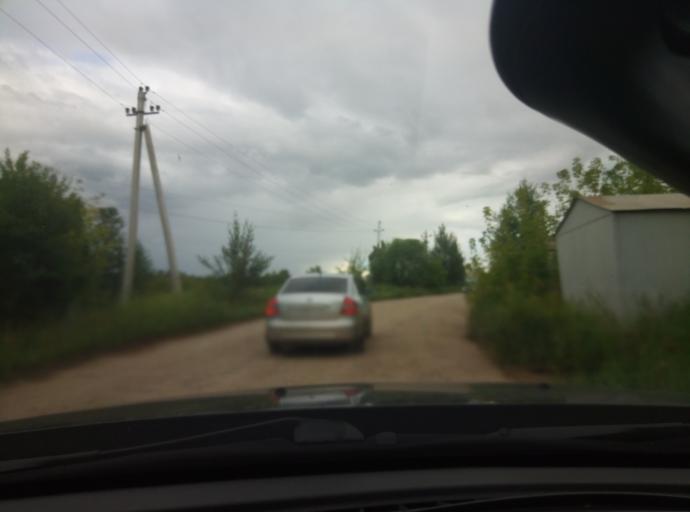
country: RU
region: Tula
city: Bolokhovo
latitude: 54.0790
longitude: 37.8188
